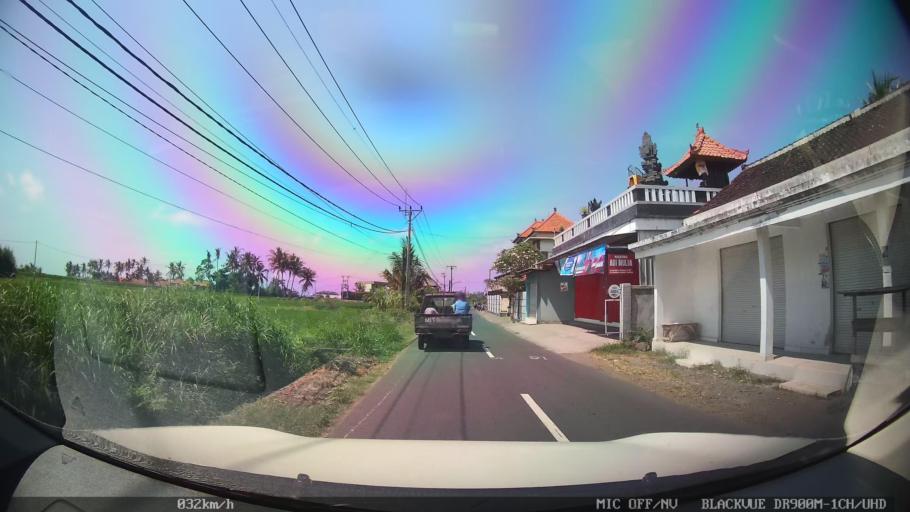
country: ID
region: Bali
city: Banjar Pasekan
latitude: -8.6098
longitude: 115.3040
